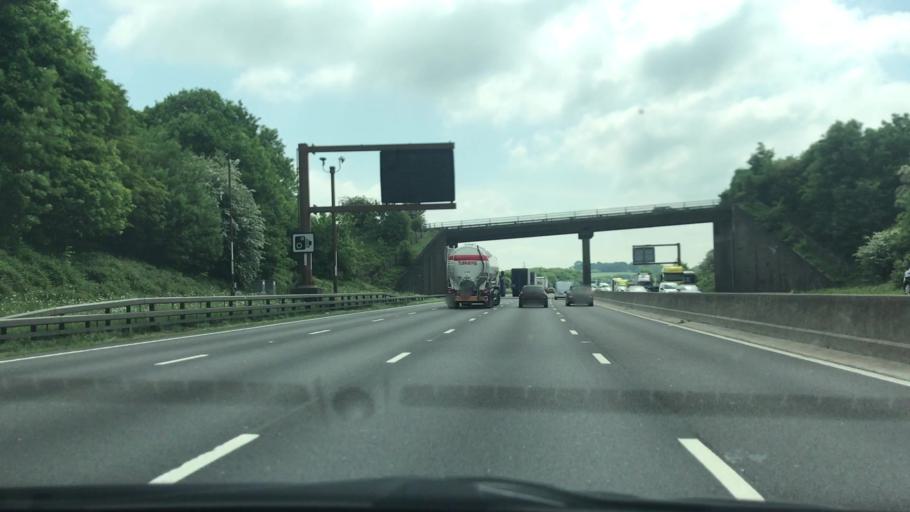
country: GB
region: England
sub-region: Derbyshire
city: Tibshelf
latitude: 53.1657
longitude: -1.3240
